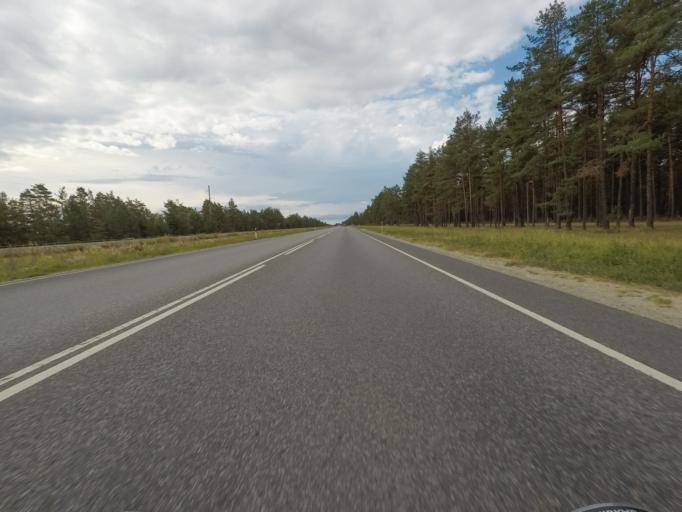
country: EE
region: Harju
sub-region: Saku vald
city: Saku
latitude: 59.3559
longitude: 24.7125
